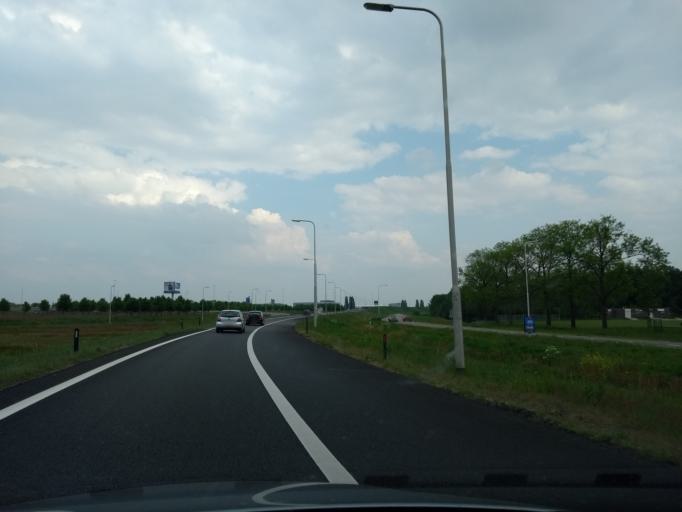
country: NL
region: Friesland
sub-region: Gemeente Heerenveen
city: Heerenveen
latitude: 52.9702
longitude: 5.9256
